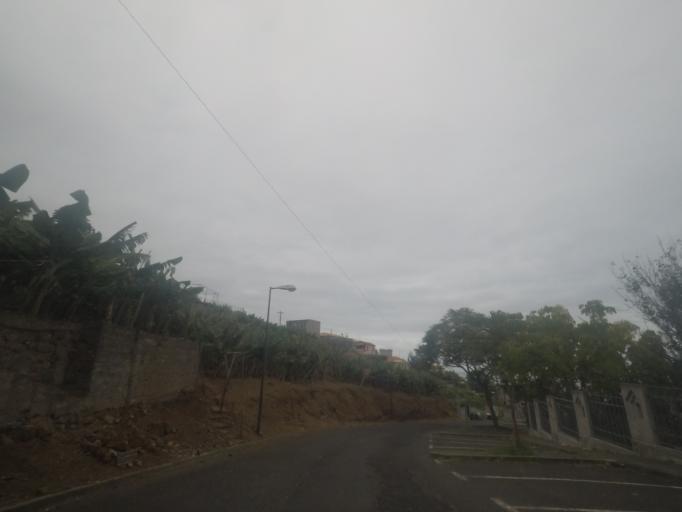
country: PT
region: Madeira
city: Camara de Lobos
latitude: 32.6538
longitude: -16.9814
